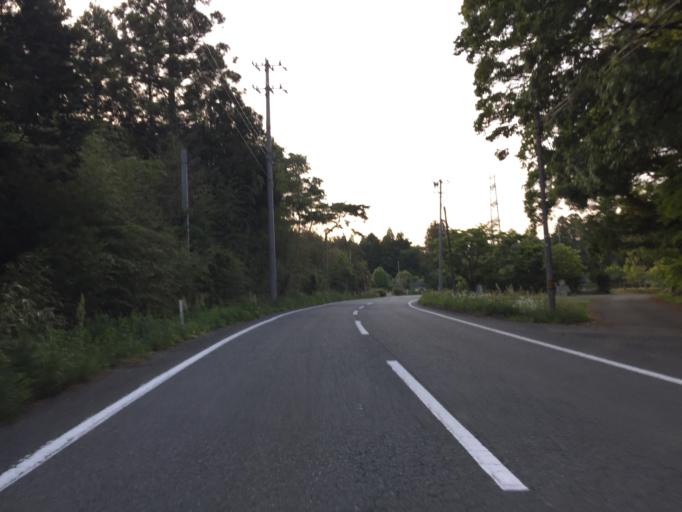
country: JP
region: Fukushima
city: Iwaki
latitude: 37.2332
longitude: 140.9772
